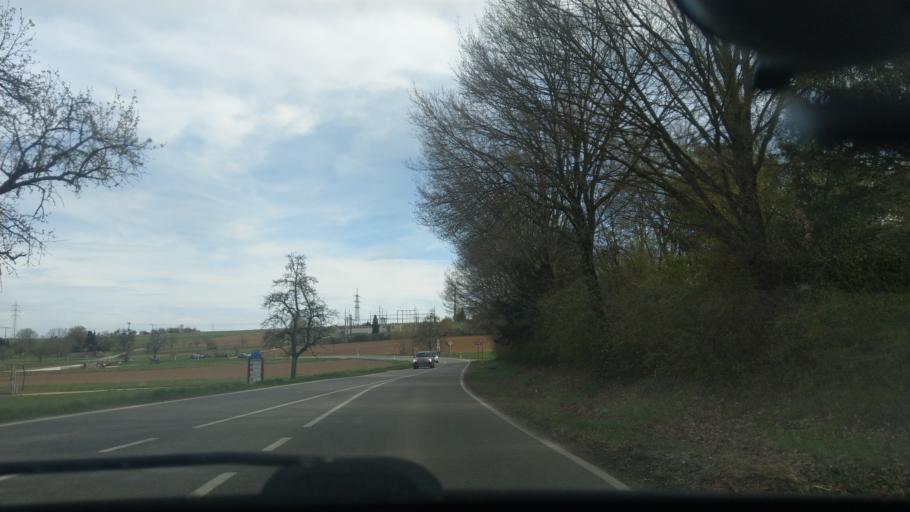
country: DE
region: Baden-Wuerttemberg
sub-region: Regierungsbezirk Stuttgart
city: Filderstadt
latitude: 48.6689
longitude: 9.2437
